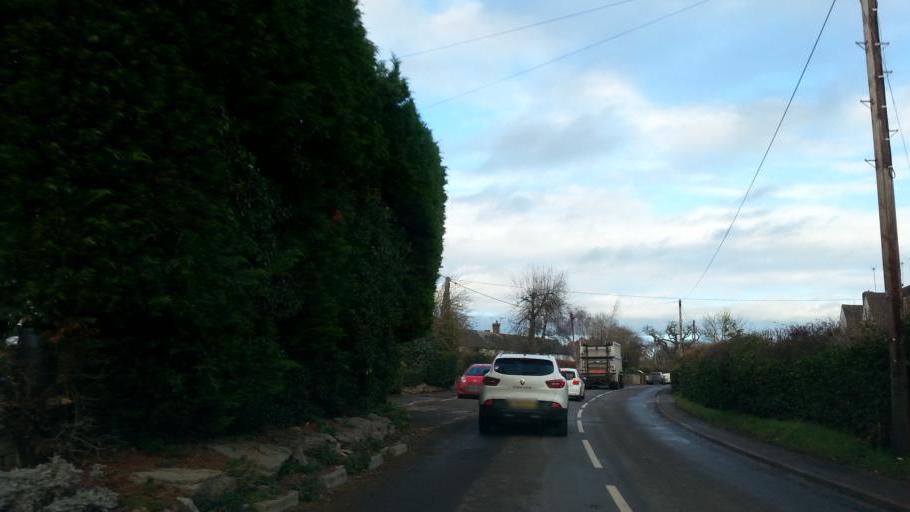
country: GB
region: England
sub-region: Oxfordshire
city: Stanford in the Vale
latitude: 51.6392
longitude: -1.5461
